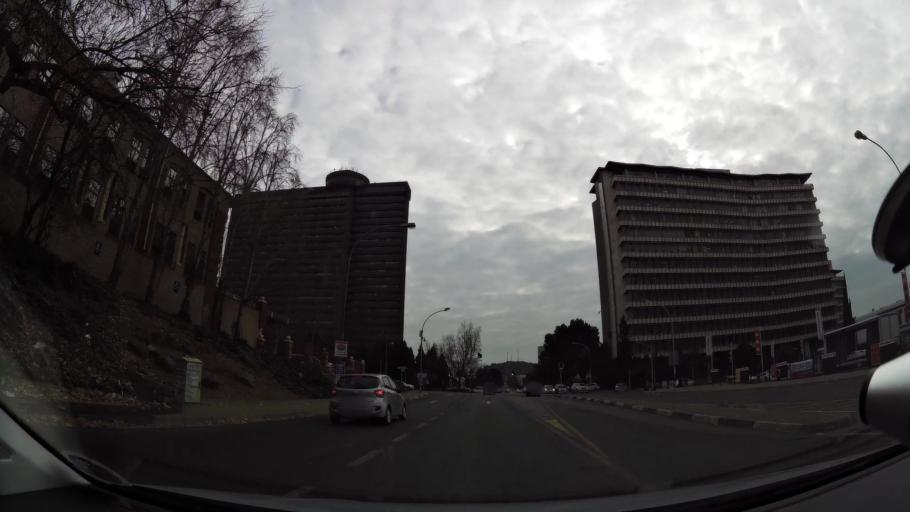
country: ZA
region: Orange Free State
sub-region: Mangaung Metropolitan Municipality
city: Bloemfontein
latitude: -29.1174
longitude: 26.2137
